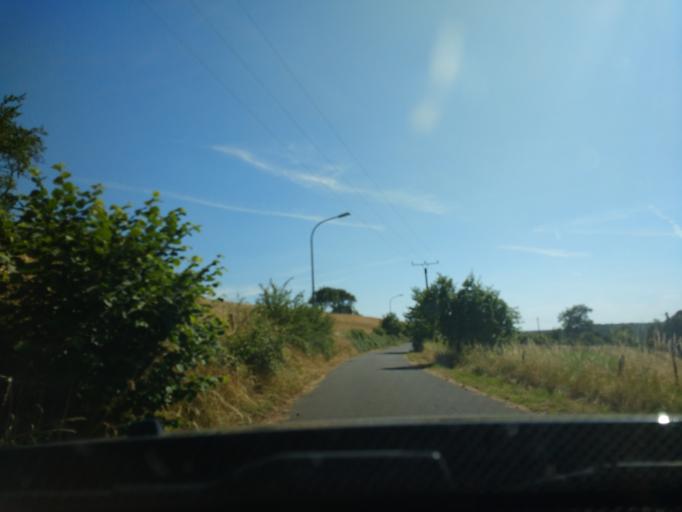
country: DE
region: Rheinland-Pfalz
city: Brockscheid
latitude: 50.1349
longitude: 6.8230
